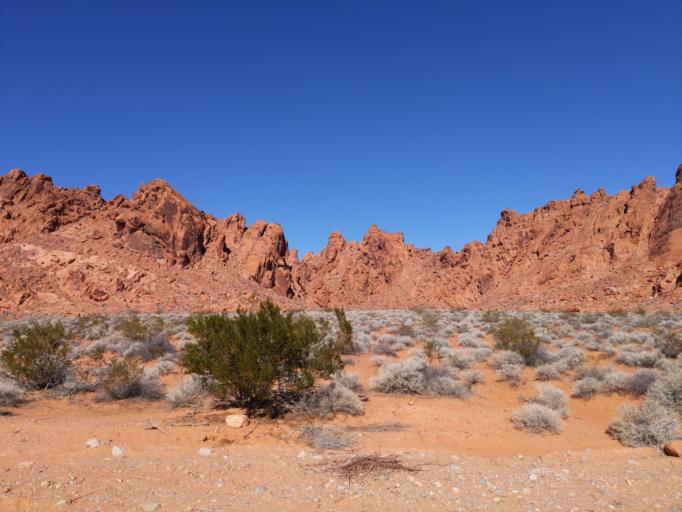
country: US
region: Nevada
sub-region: Clark County
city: Moapa Valley
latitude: 36.4276
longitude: -114.4985
